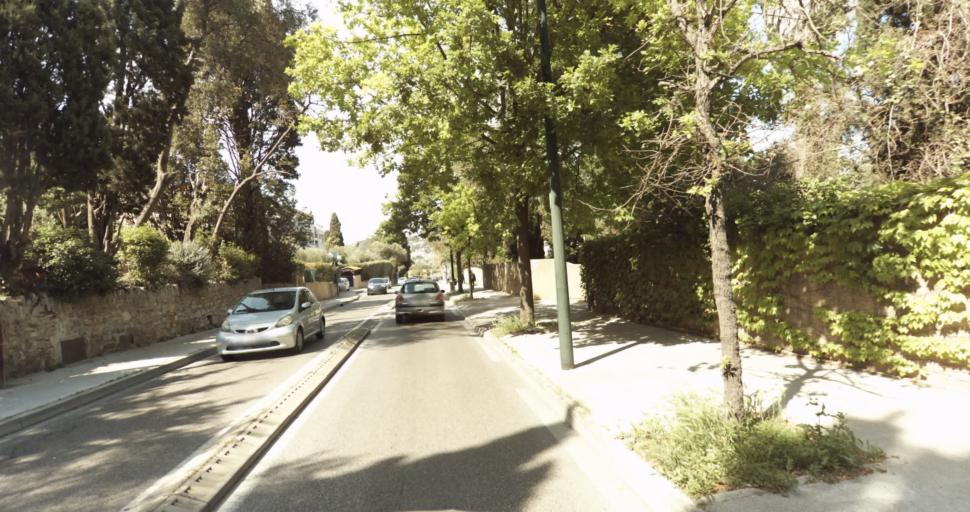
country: FR
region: Provence-Alpes-Cote d'Azur
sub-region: Departement du Var
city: Hyeres
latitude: 43.1043
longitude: 6.1216
